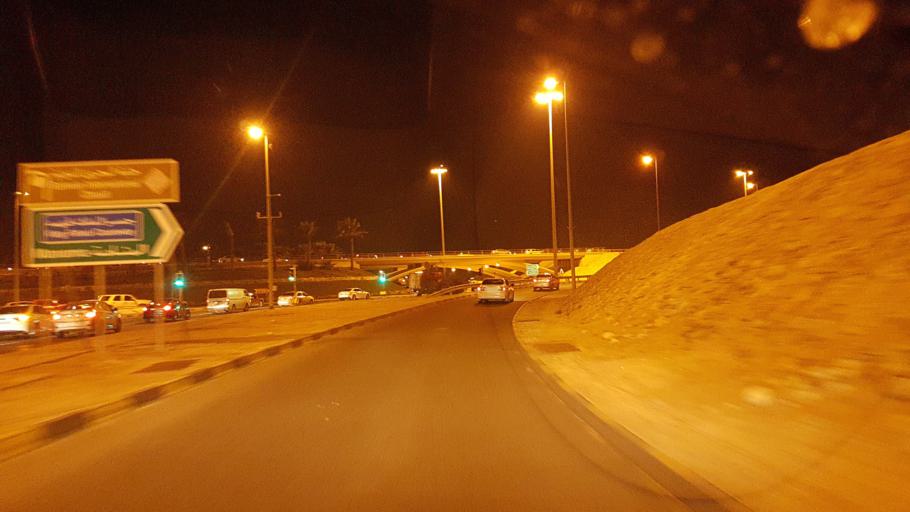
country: BH
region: Central Governorate
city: Madinat Hamad
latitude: 26.1398
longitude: 50.5122
